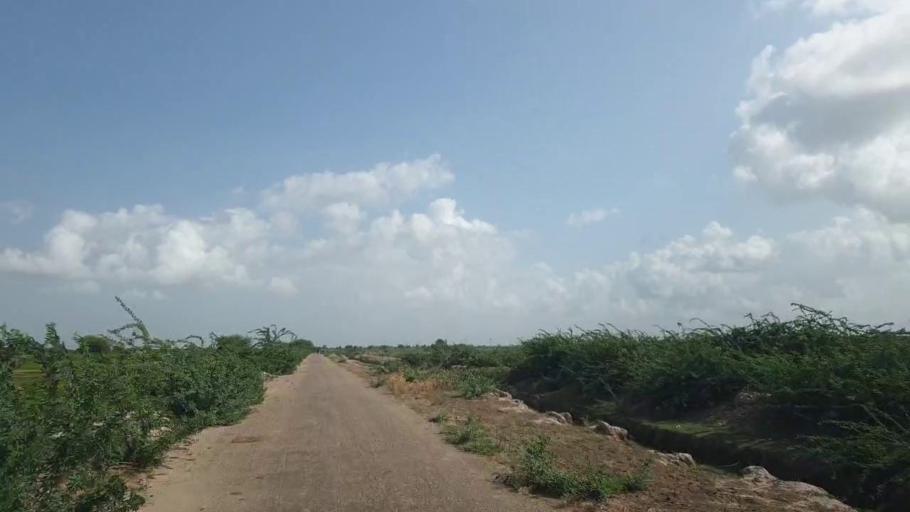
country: PK
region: Sindh
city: Kadhan
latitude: 24.5738
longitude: 69.0671
